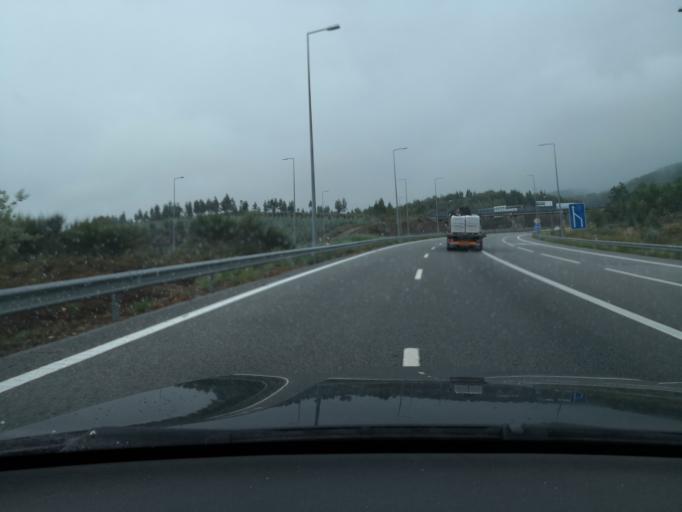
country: PT
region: Porto
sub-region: Valongo
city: Sobrado
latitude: 41.2324
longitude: -8.4532
